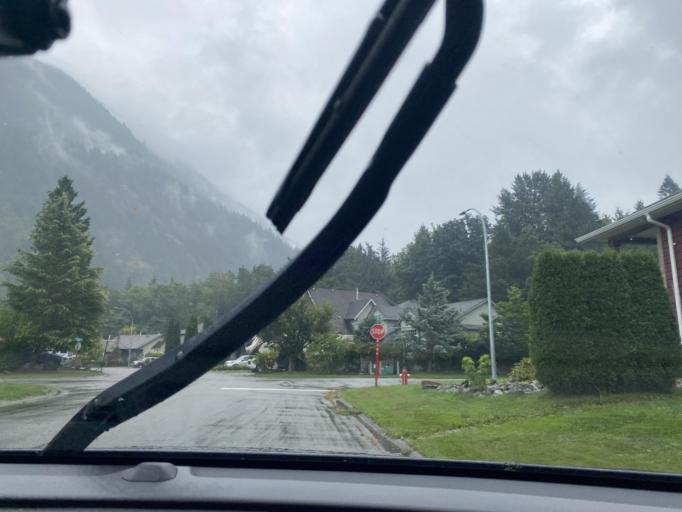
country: CA
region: British Columbia
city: Agassiz
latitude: 49.2985
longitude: -121.7767
